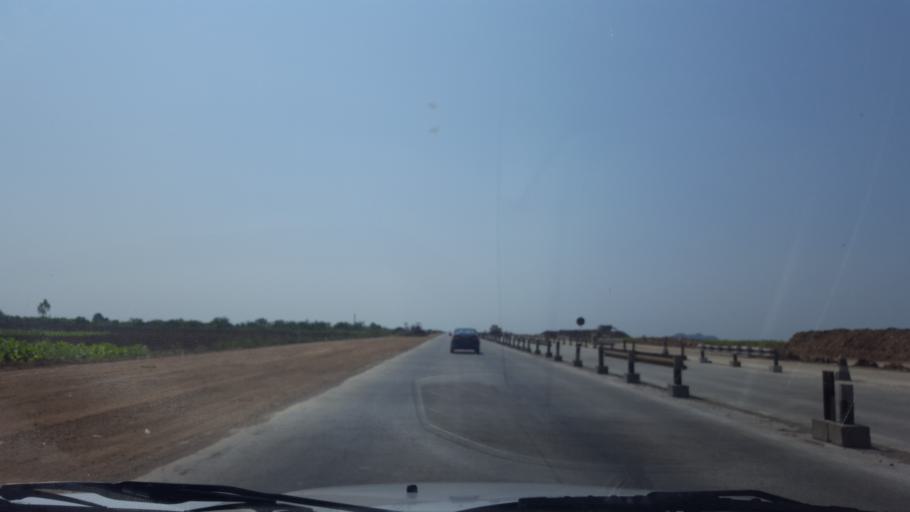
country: IN
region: Andhra Pradesh
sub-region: Prakasam
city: Addanki
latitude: 15.7862
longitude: 80.0373
